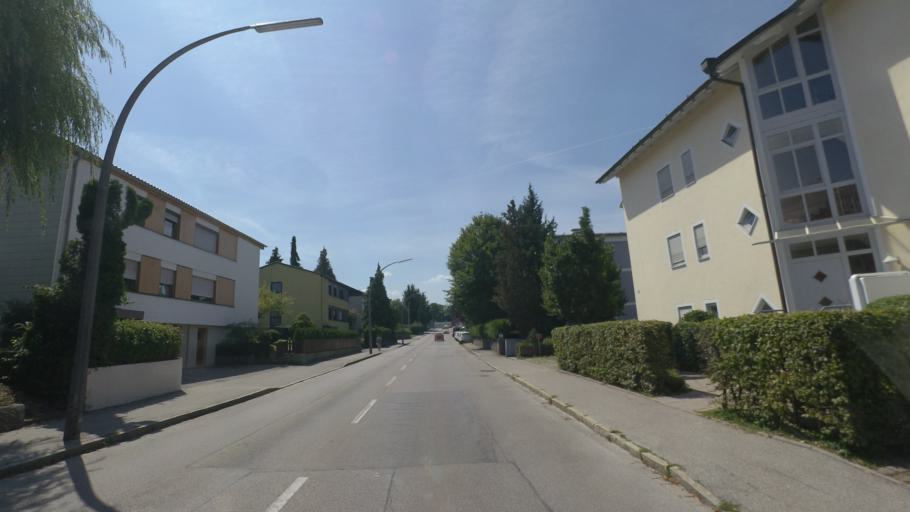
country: DE
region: Bavaria
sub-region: Upper Bavaria
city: Traunstein
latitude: 47.8692
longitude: 12.6332
